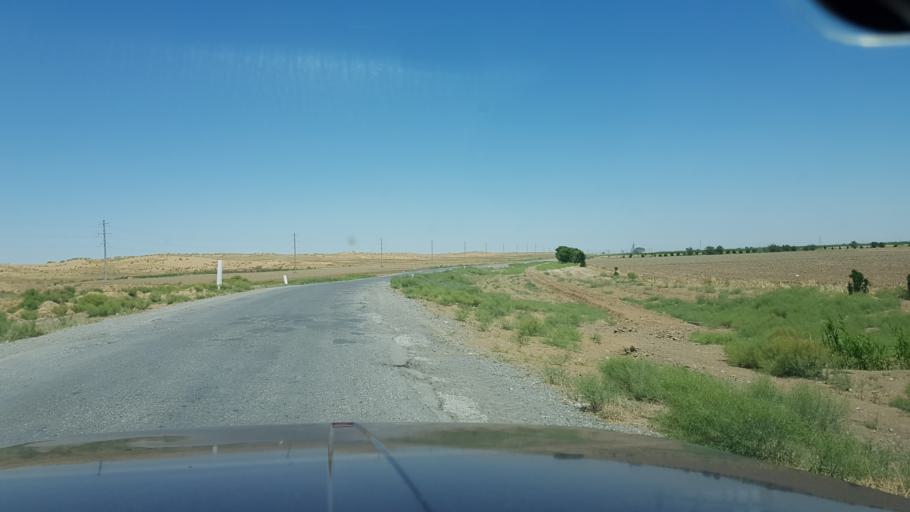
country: TM
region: Ahal
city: Annau
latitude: 37.8575
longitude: 58.7075
